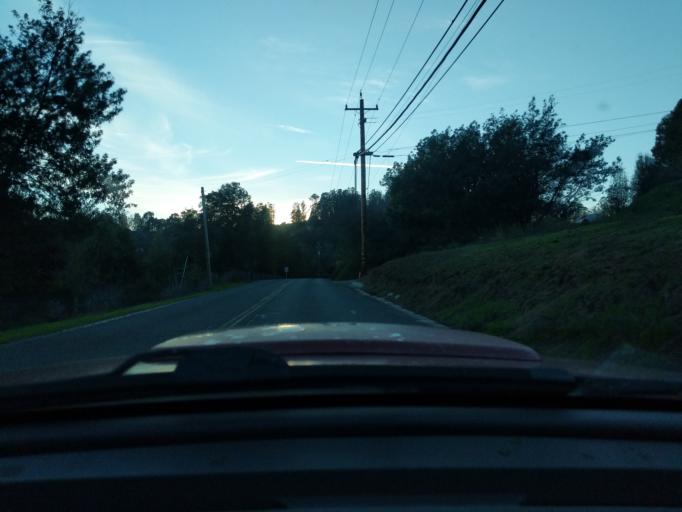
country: US
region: California
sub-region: Monterey County
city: Prunedale
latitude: 36.8226
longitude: -121.6710
